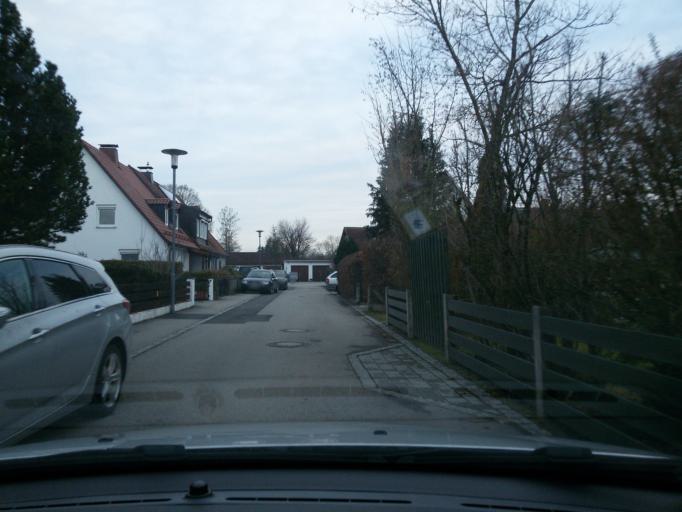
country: DE
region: Bavaria
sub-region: Swabia
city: Klosterlechfeld
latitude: 48.1589
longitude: 10.8348
